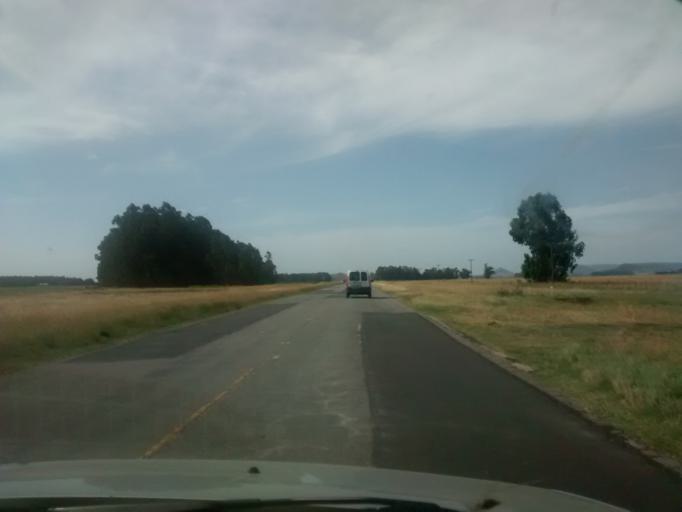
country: AR
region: Buenos Aires
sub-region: Partido de Loberia
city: Loberia
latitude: -37.9640
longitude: -58.6893
